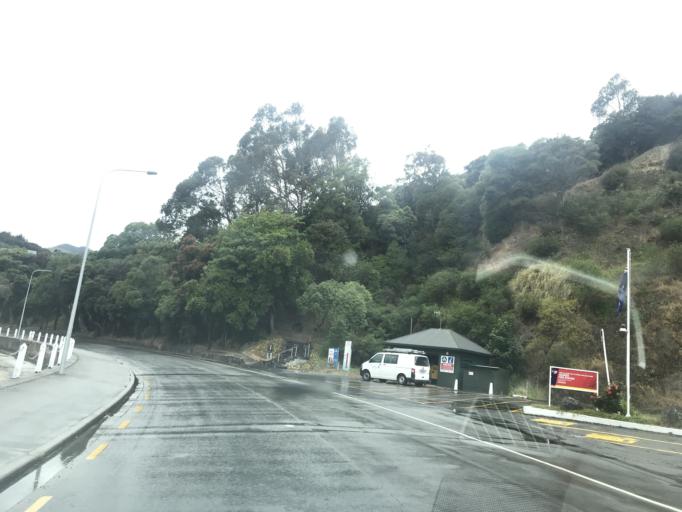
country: NZ
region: Canterbury
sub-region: Christchurch City
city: Christchurch
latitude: -43.8084
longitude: 172.9646
